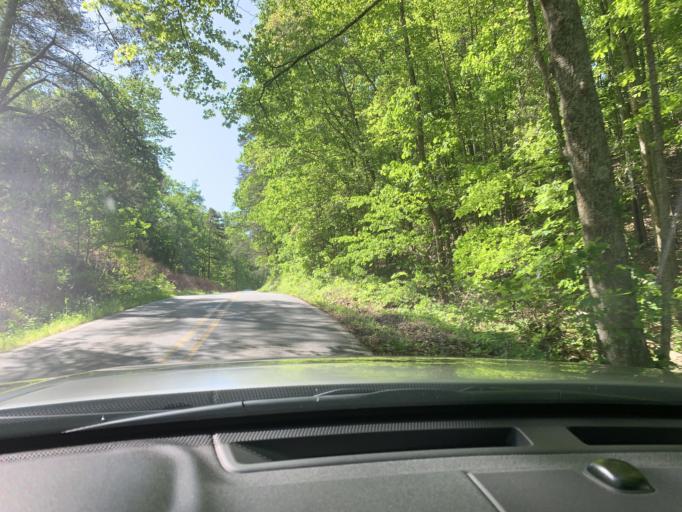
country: US
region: Georgia
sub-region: Haralson County
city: Buchanan
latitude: 33.9213
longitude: -85.2047
